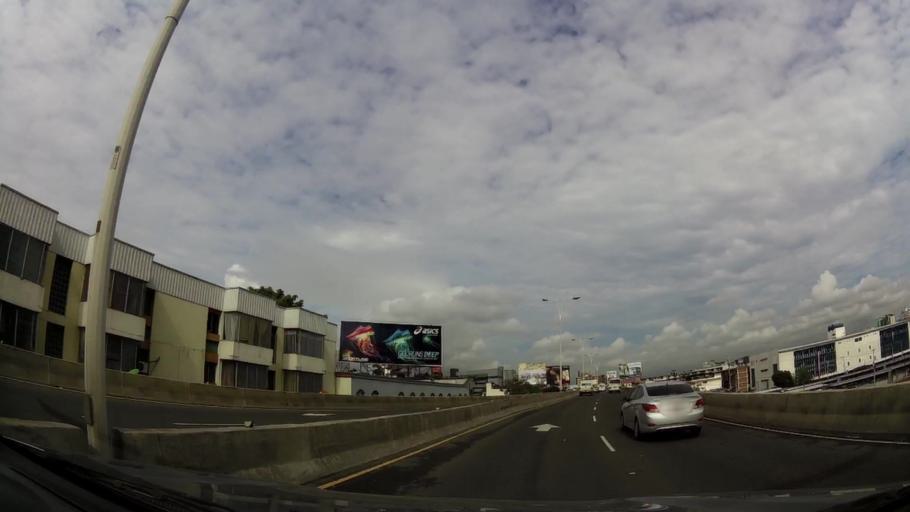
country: PA
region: Panama
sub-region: Distrito de Panama
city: Ancon
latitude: 8.9604
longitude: -79.5391
